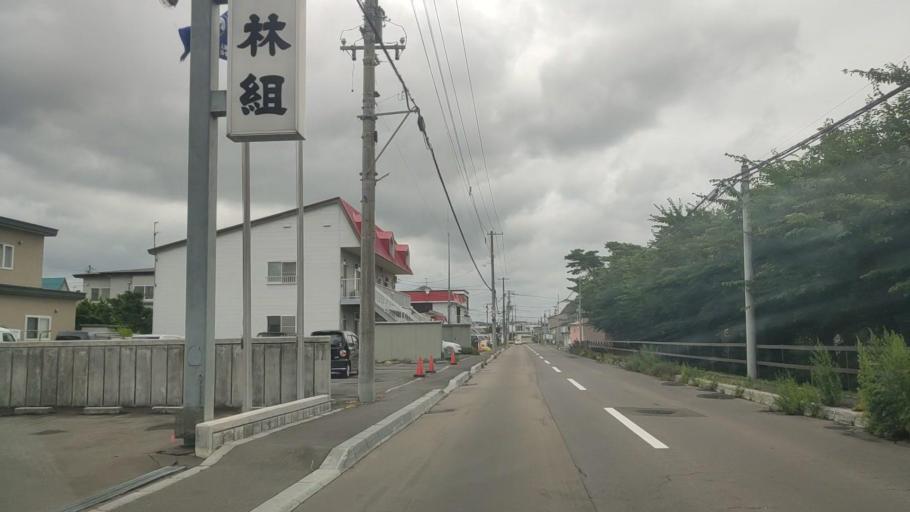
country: JP
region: Hokkaido
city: Hakodate
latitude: 41.7994
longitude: 140.7578
